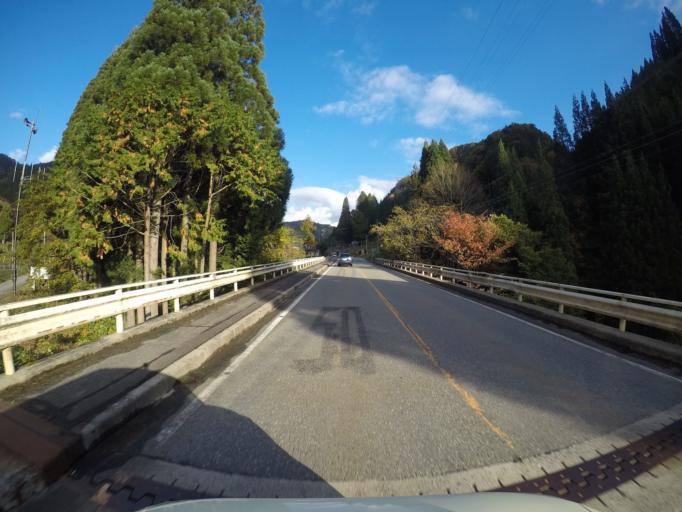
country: JP
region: Gifu
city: Takayama
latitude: 36.1773
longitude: 137.4062
